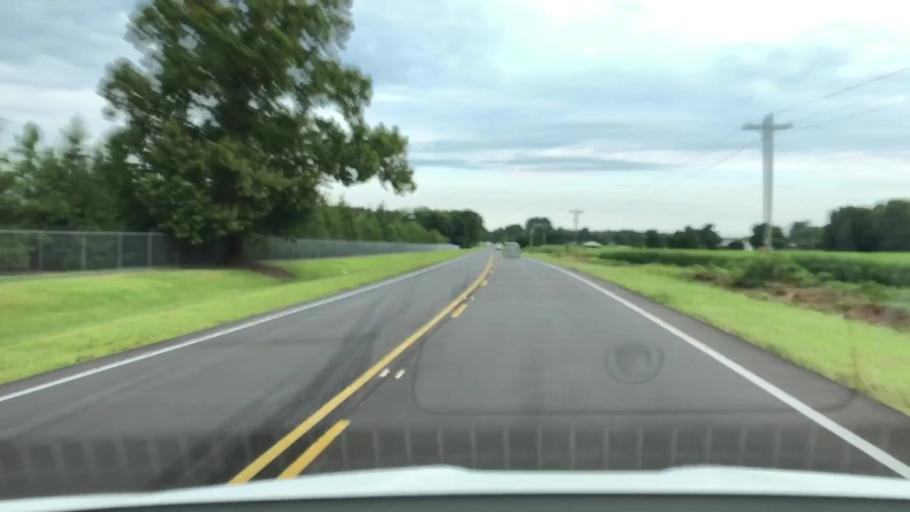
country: US
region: North Carolina
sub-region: Jones County
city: Maysville
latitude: 34.8927
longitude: -77.2162
